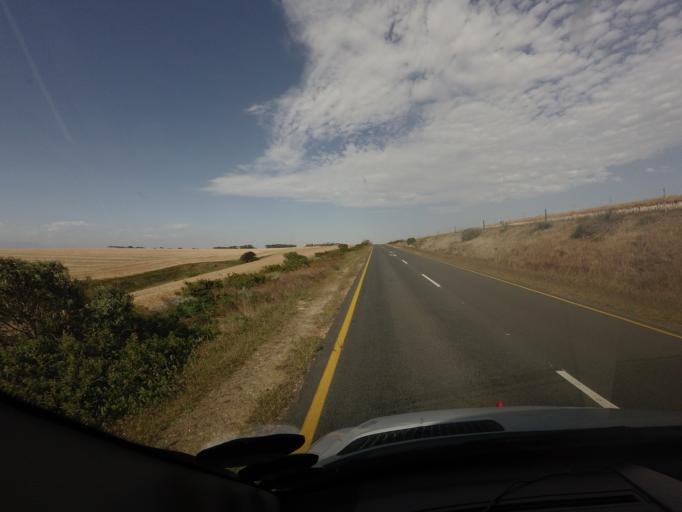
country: ZA
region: Western Cape
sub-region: Overberg District Municipality
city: Caledon
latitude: -34.3289
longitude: 19.7332
